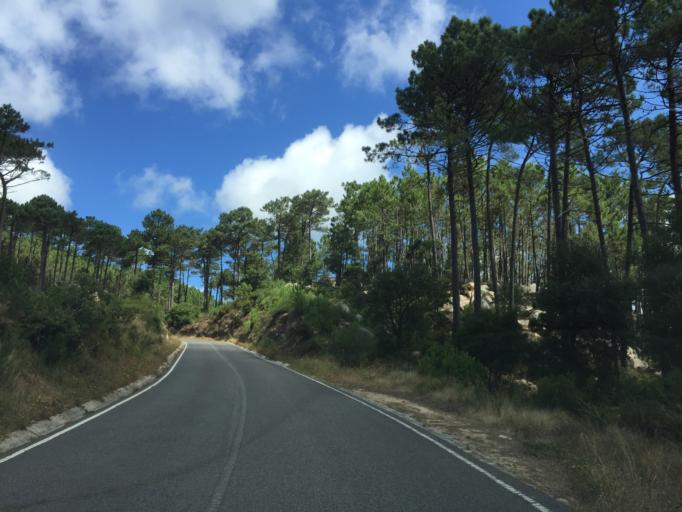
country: PT
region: Lisbon
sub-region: Cascais
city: Alcabideche
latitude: 38.7576
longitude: -9.4277
